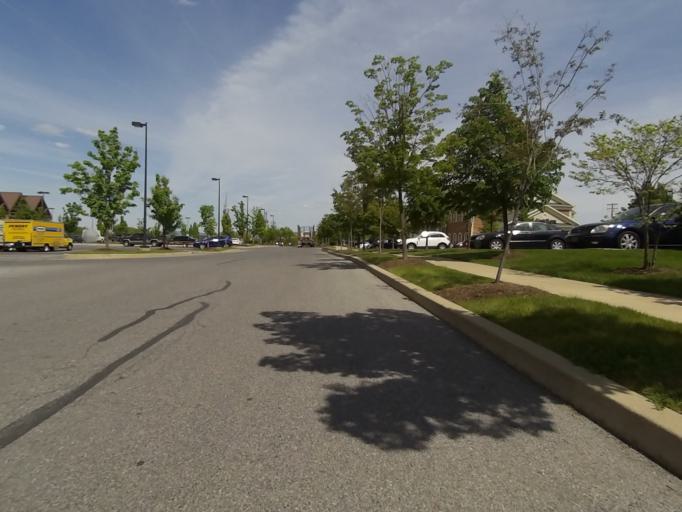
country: US
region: Pennsylvania
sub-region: Centre County
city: Park Forest Village
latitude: 40.8134
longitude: -77.9242
